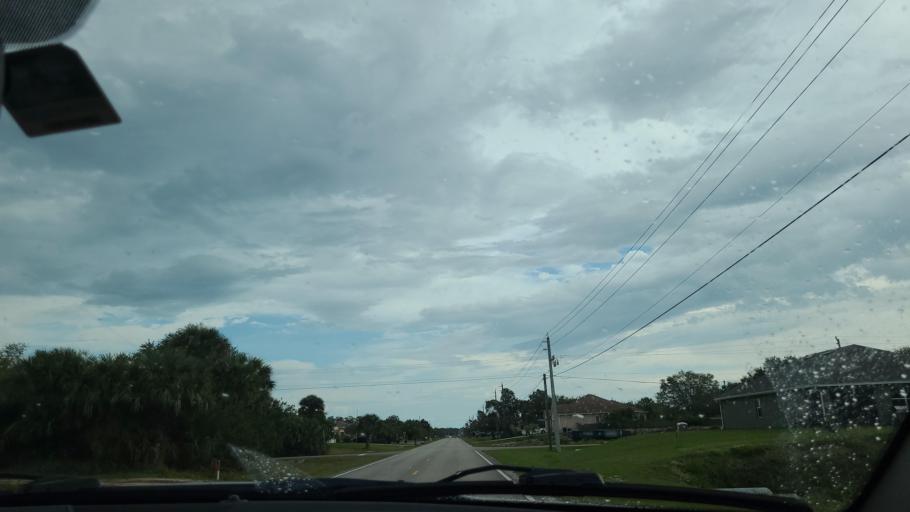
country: US
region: Florida
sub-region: Brevard County
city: Grant-Valkaria
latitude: 27.9528
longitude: -80.6887
